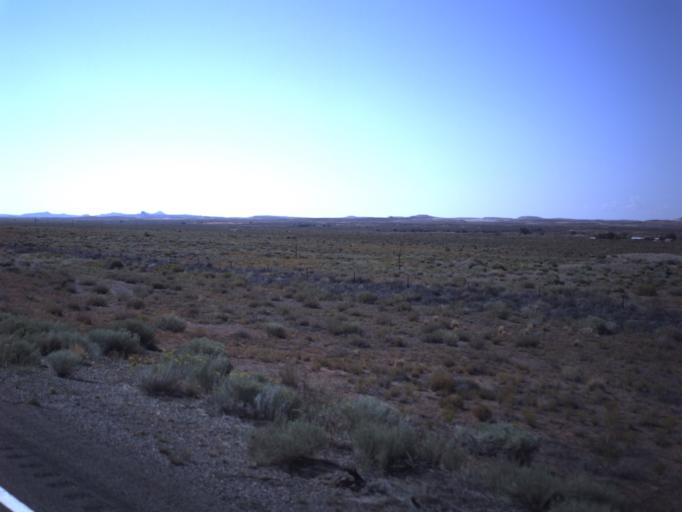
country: US
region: Utah
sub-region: San Juan County
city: Blanding
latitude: 37.1539
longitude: -109.5685
